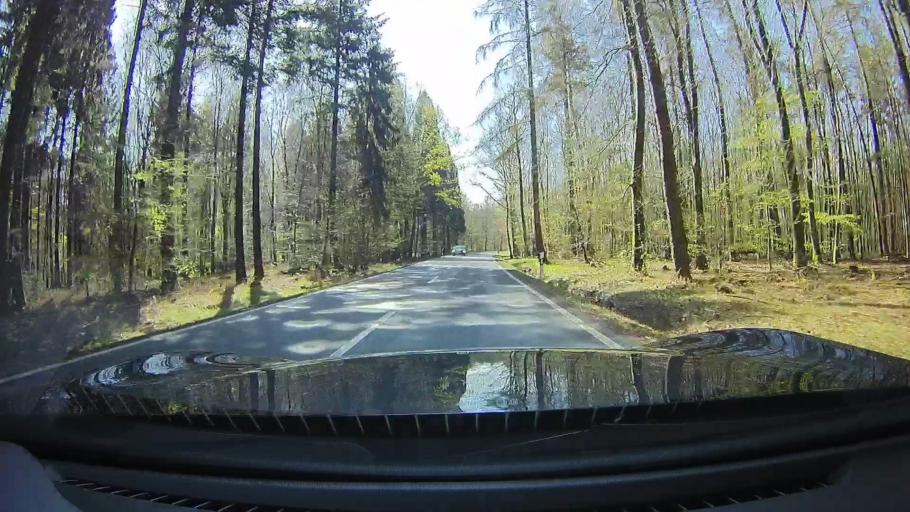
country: DE
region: Baden-Wuerttemberg
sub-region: Karlsruhe Region
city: Neunkirchen
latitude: 49.4166
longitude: 8.9833
